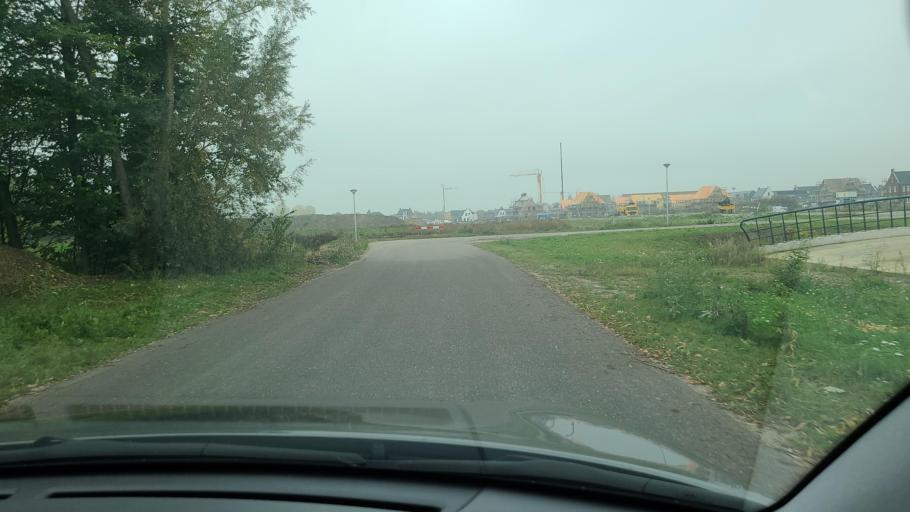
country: NL
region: Gelderland
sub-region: Gemeente Geldermalsen
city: Geldermalsen
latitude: 51.8667
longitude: 5.2967
